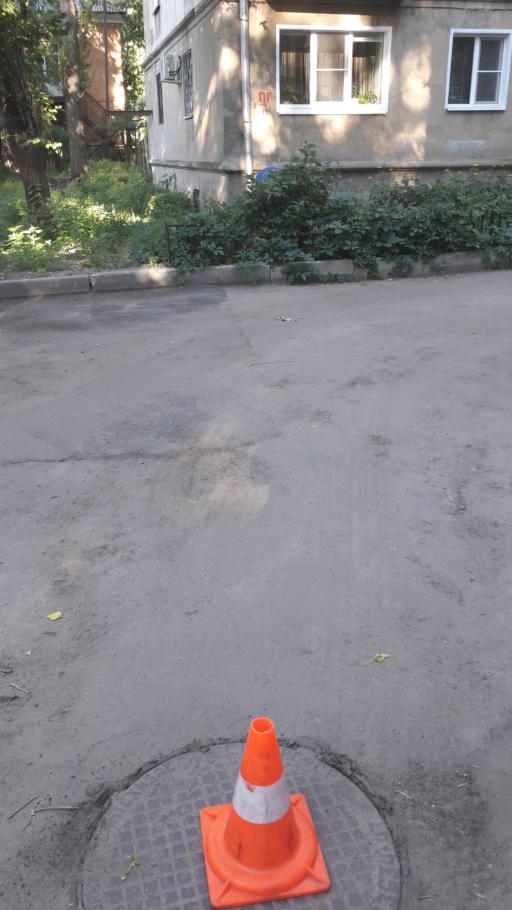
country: RU
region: Voronezj
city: Voronezh
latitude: 51.6761
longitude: 39.1935
